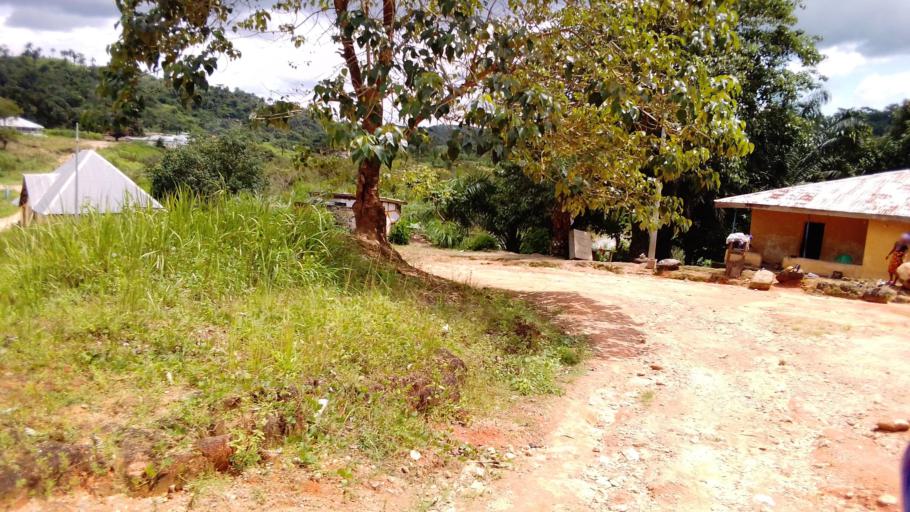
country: SL
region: Eastern Province
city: Koyima
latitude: 8.7001
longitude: -11.0126
